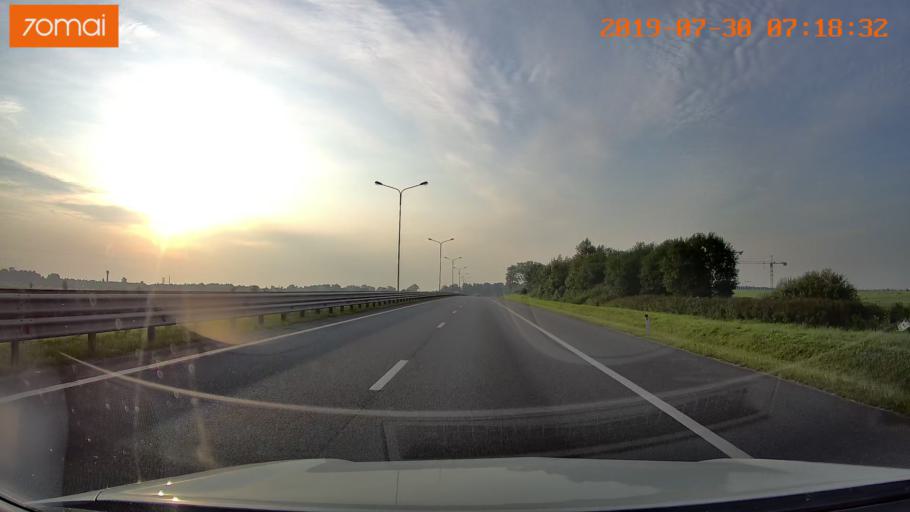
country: RU
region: Kaliningrad
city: Bol'shoe Isakovo
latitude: 54.7036
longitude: 20.6506
